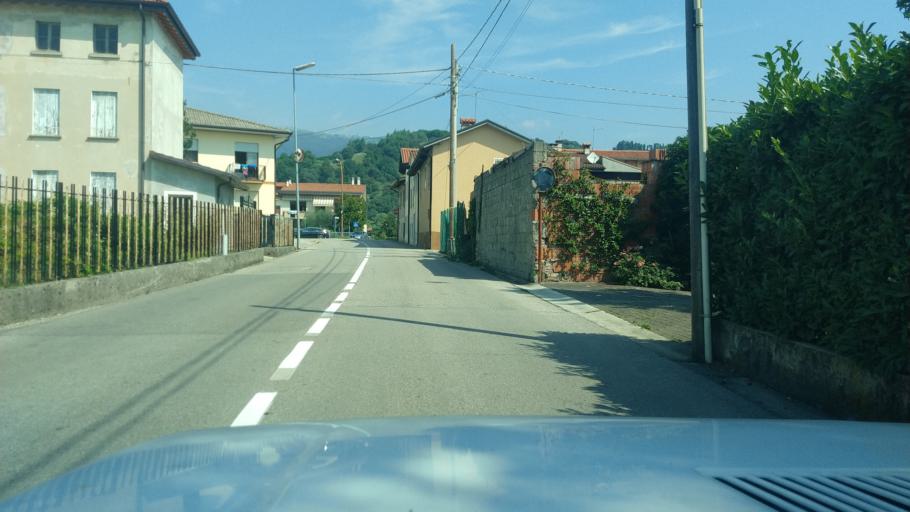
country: IT
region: Veneto
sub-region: Provincia di Vicenza
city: Marostica
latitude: 45.7482
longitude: 11.6687
